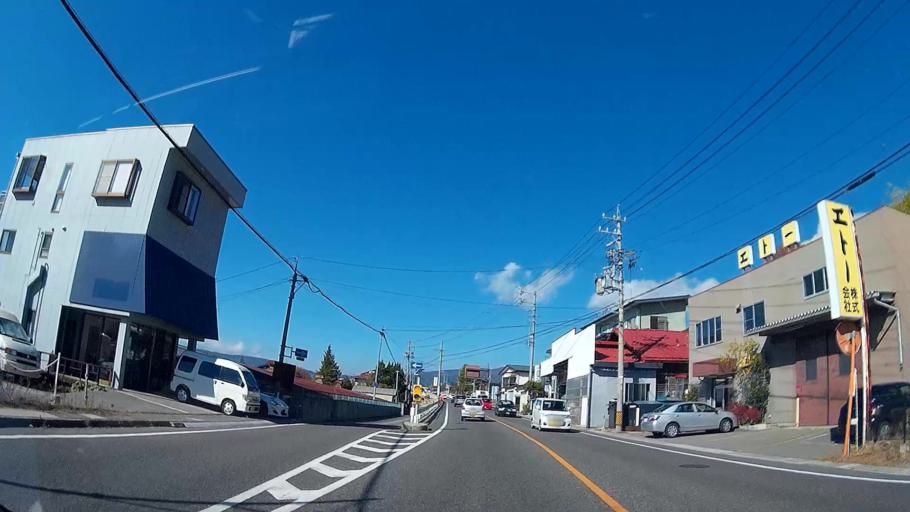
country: JP
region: Nagano
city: Suwa
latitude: 36.0679
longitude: 138.0989
